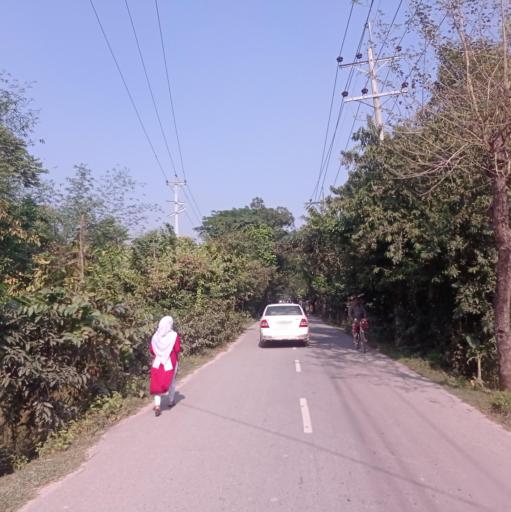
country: BD
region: Dhaka
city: Narsingdi
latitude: 24.0700
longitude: 90.6924
